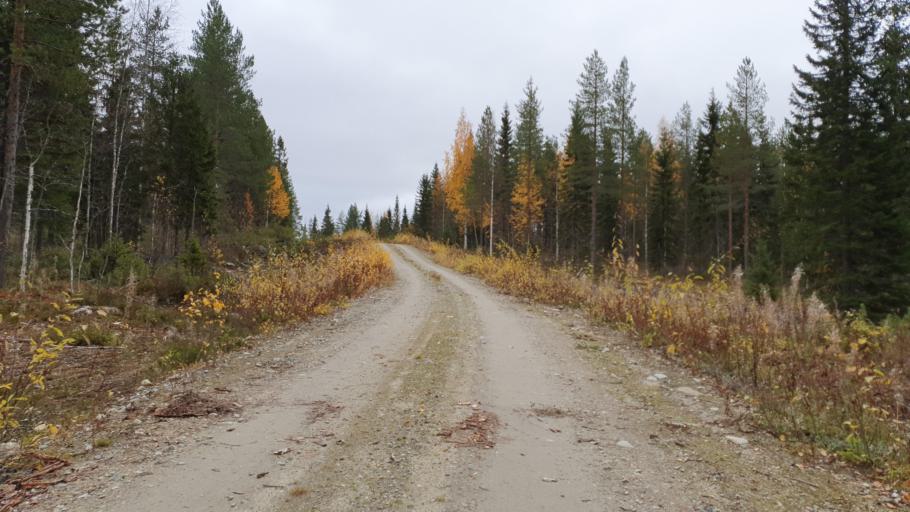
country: FI
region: Kainuu
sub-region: Kehys-Kainuu
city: Kuhmo
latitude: 64.4449
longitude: 29.6284
